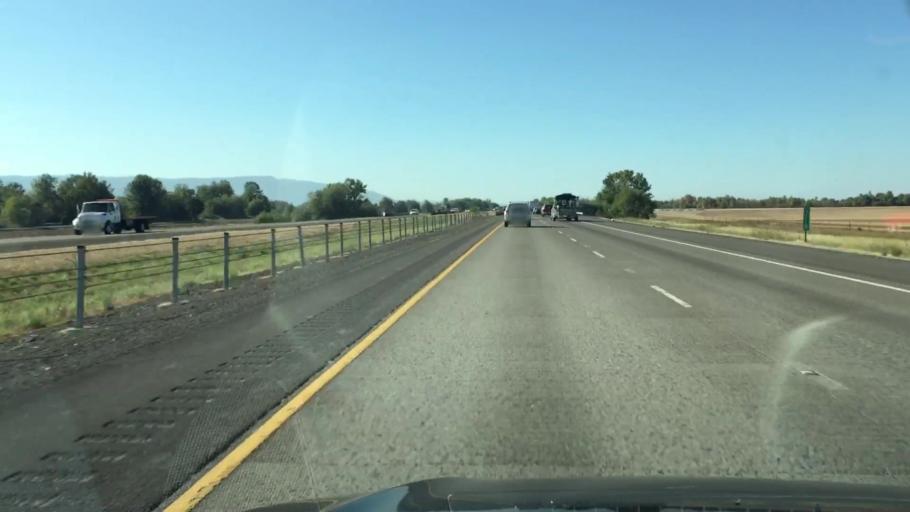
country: US
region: Oregon
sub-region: Linn County
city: Brownsville
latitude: 44.4096
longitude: -123.0609
